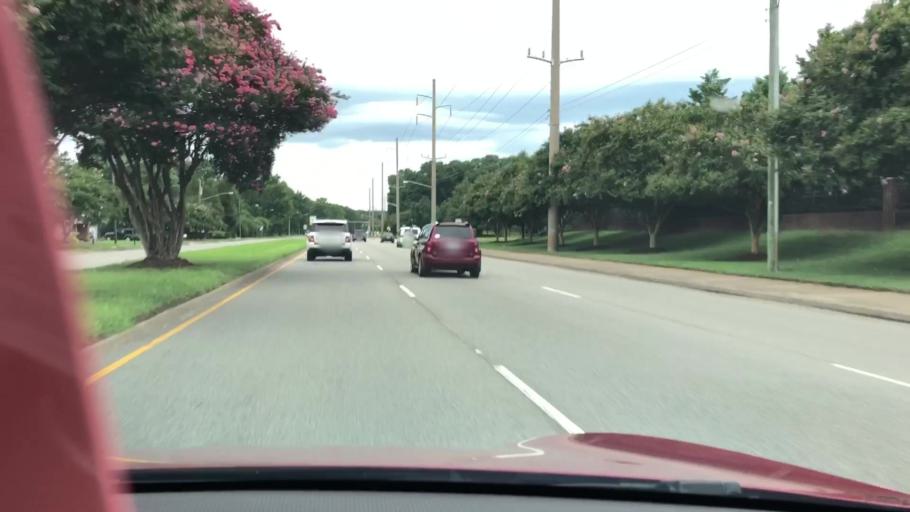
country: US
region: Virginia
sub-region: City of Virginia Beach
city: Virginia Beach
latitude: 36.8826
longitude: -76.0456
